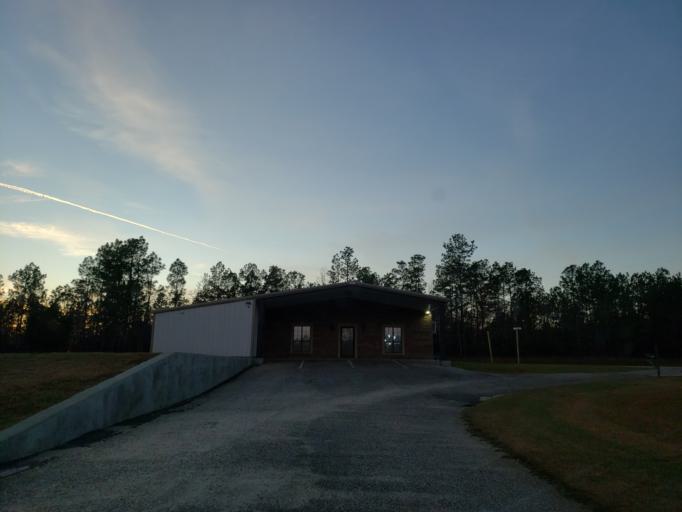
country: US
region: Mississippi
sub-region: Lamar County
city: West Hattiesburg
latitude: 31.2491
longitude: -89.3330
